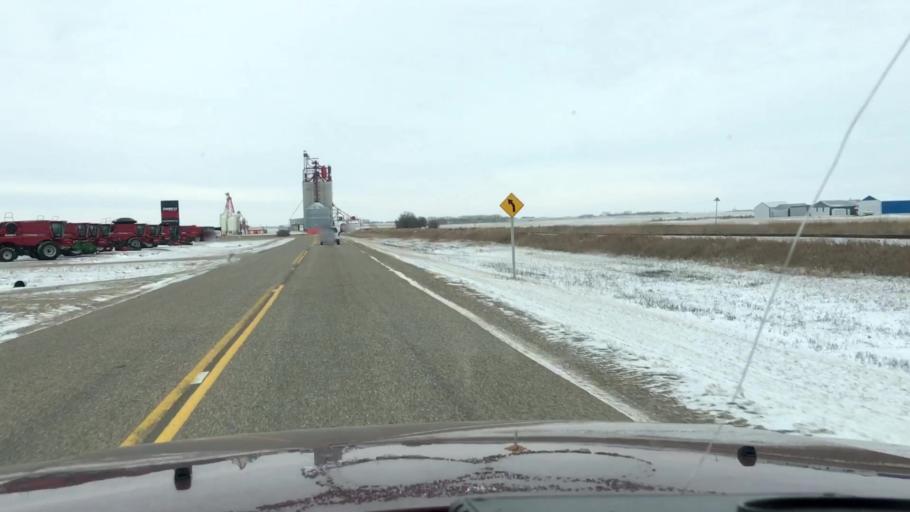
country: CA
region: Saskatchewan
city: Watrous
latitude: 51.2514
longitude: -105.9791
